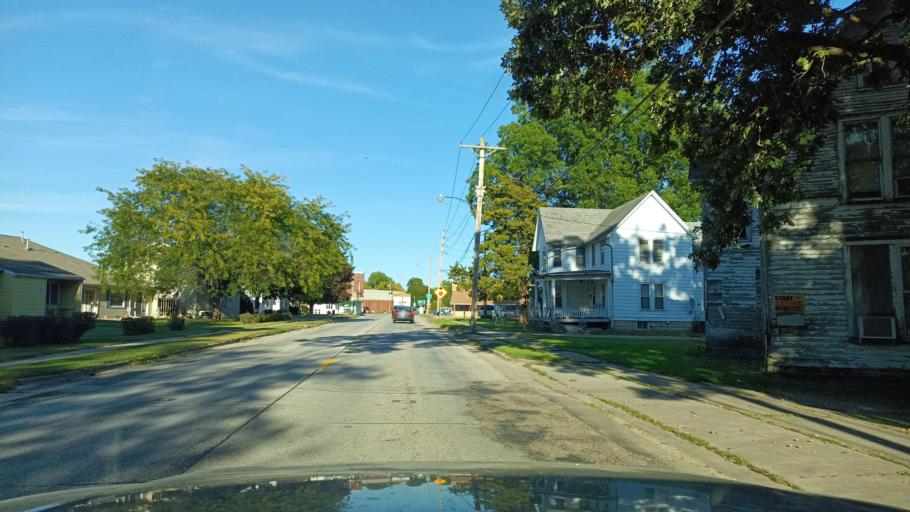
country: US
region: Illinois
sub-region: De Witt County
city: Farmer City
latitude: 40.2411
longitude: -88.6444
